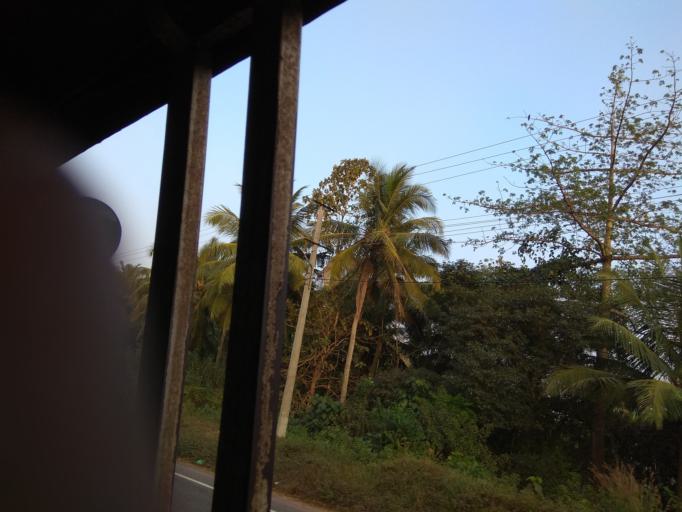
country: IN
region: Karnataka
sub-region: Dakshina Kannada
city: Mangalore
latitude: 12.9374
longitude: 74.8629
